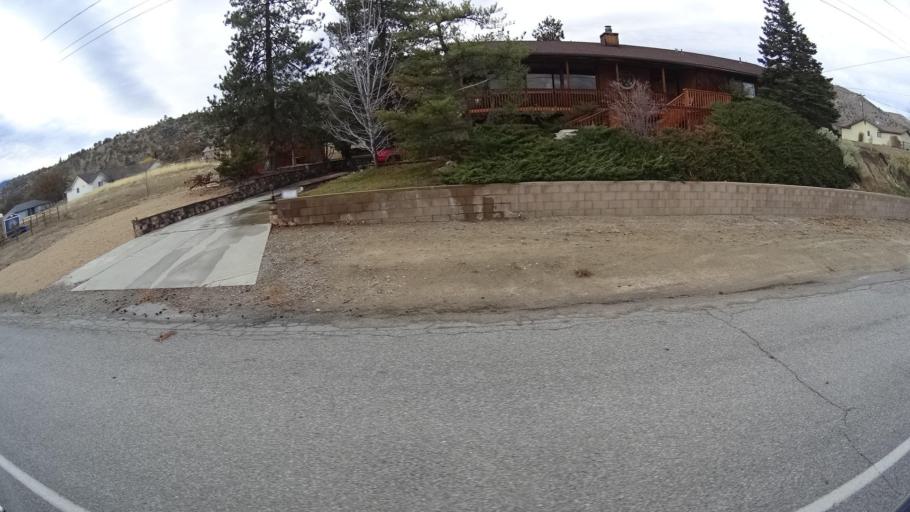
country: US
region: California
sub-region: Kern County
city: Golden Hills
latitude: 35.1401
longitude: -118.5062
